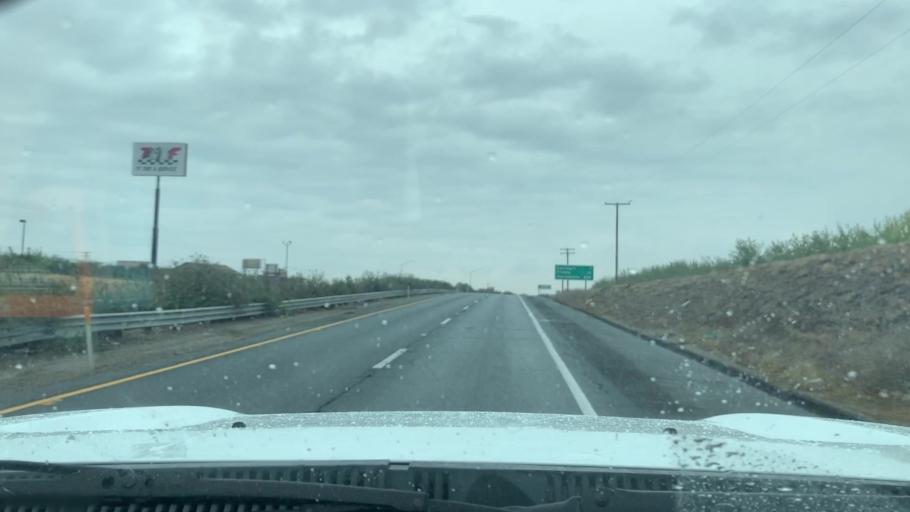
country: US
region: California
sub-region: Kern County
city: Delano
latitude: 35.7918
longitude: -119.2515
